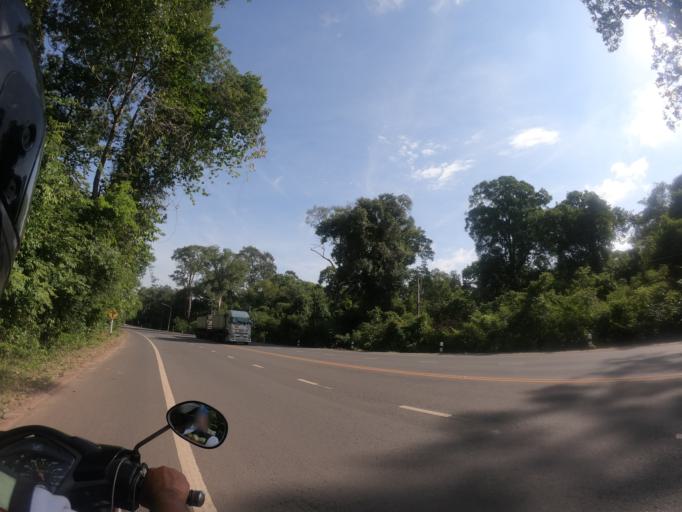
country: TH
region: Surin
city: Kap Choeng
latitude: 14.4493
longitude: 103.7002
